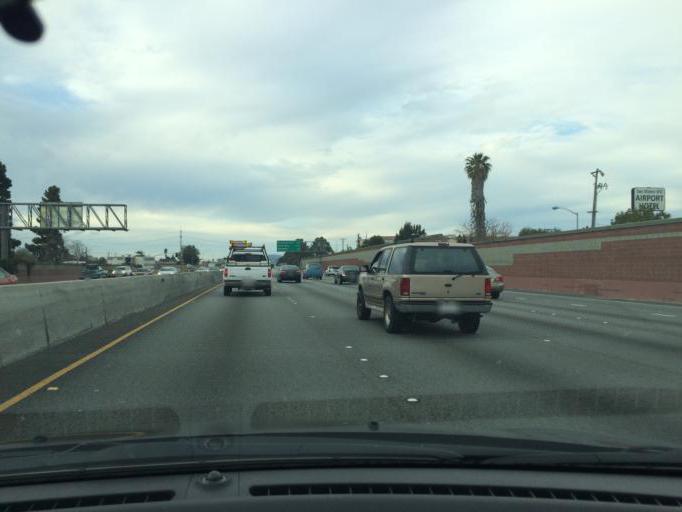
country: US
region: California
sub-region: San Mateo County
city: San Mateo
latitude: 37.5787
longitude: -122.3224
